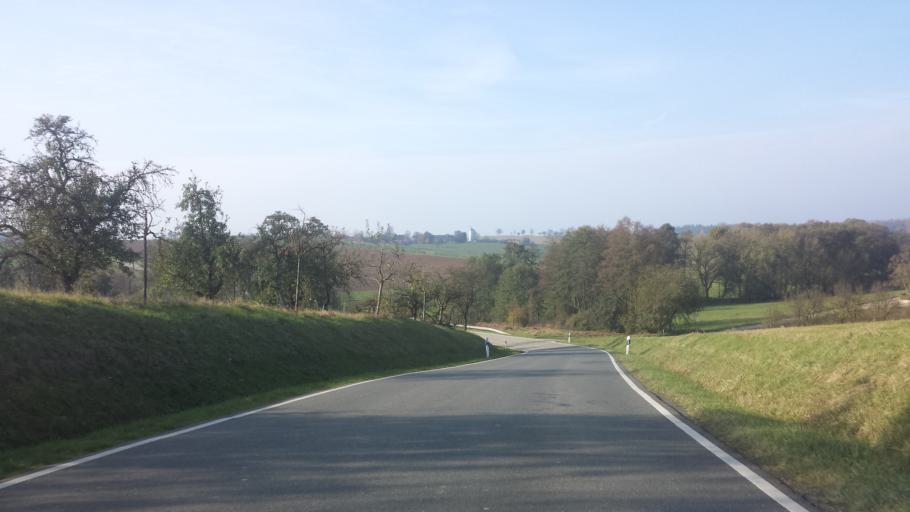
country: DE
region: Baden-Wuerttemberg
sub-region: Karlsruhe Region
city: Reichartshausen
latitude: 49.3300
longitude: 8.9563
